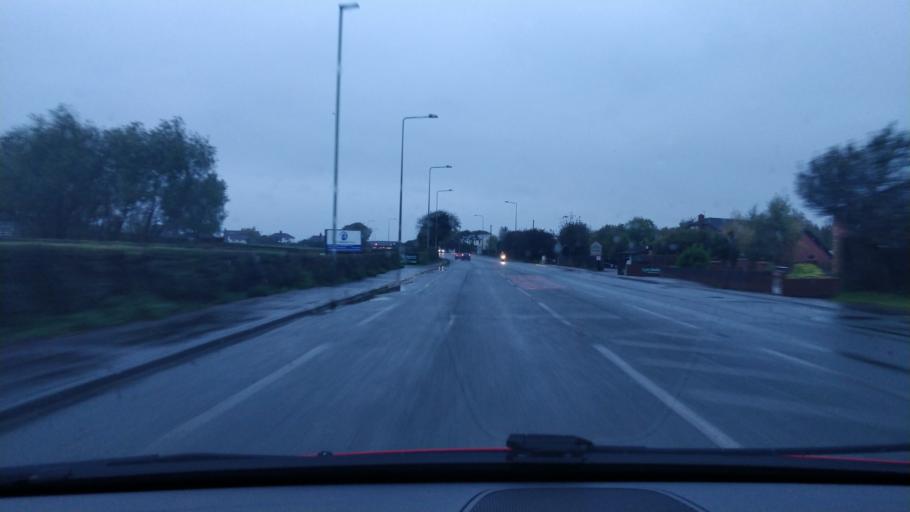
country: GB
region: England
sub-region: Lancashire
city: Poulton le Fylde
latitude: 53.7872
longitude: -2.9732
